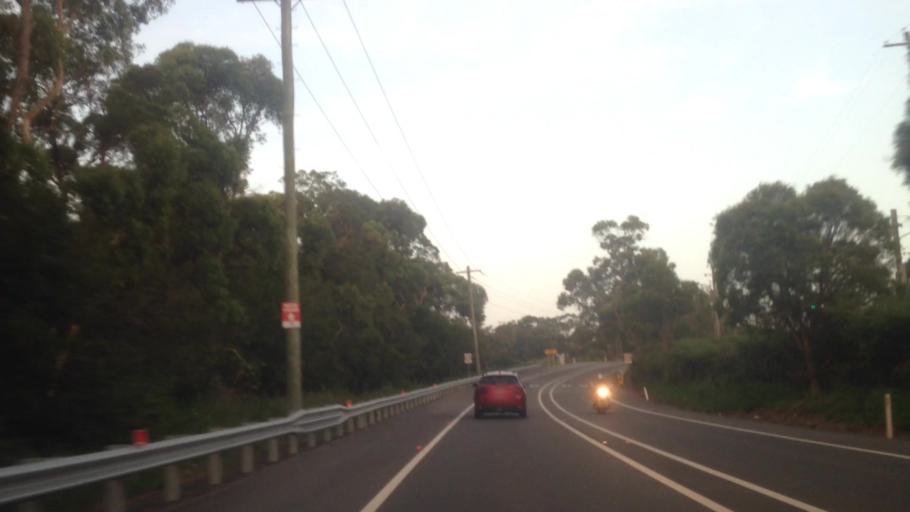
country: AU
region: New South Wales
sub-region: Lake Macquarie Shire
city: Dora Creek
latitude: -33.0992
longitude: 151.4996
